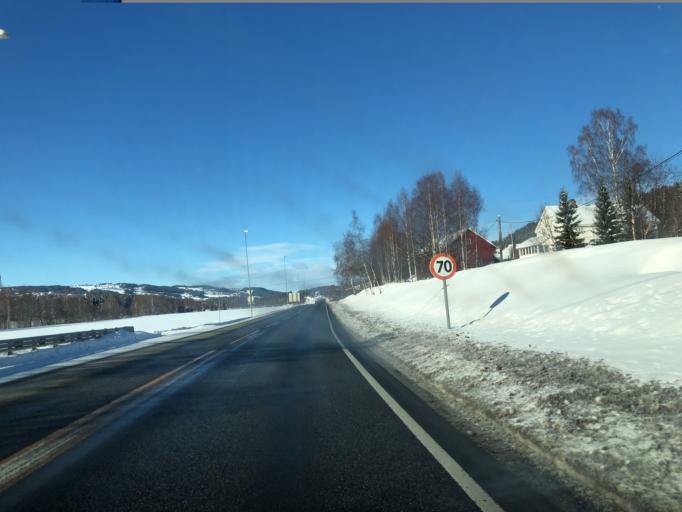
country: NO
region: Oppland
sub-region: Lunner
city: Roa
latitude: 60.2966
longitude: 10.6081
